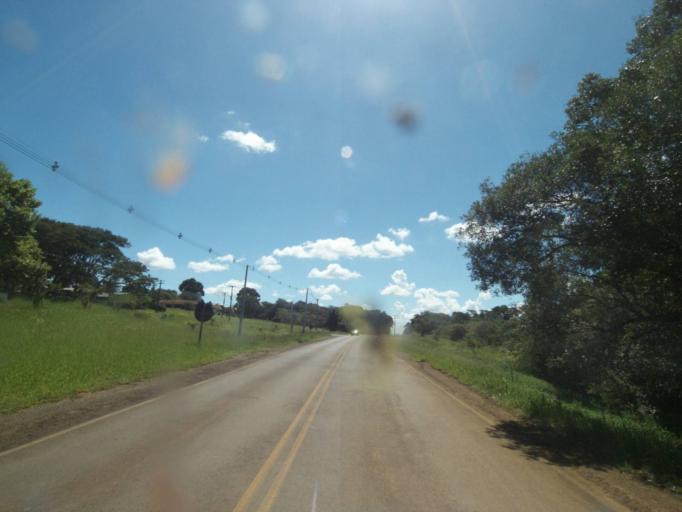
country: BR
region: Parana
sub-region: Pinhao
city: Pinhao
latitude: -25.7917
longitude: -52.0870
